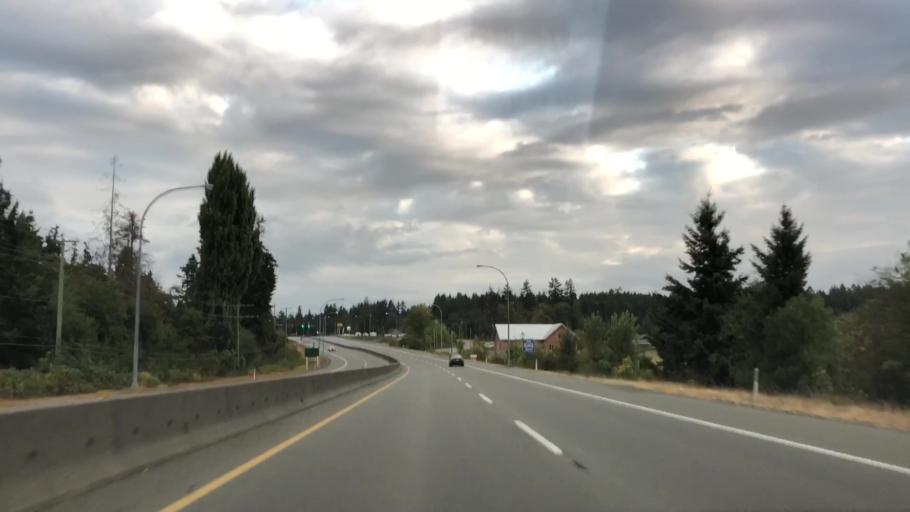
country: CA
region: British Columbia
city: North Saanich
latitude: 48.6603
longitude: -123.5600
